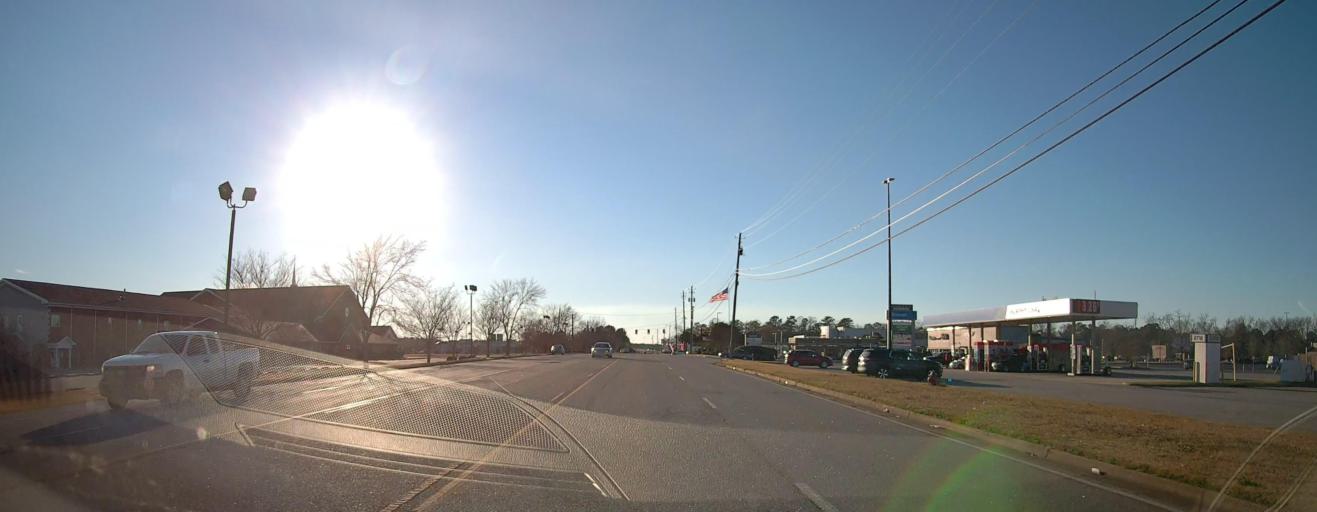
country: US
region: Georgia
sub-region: Dougherty County
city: Albany
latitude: 31.6226
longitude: -84.2140
